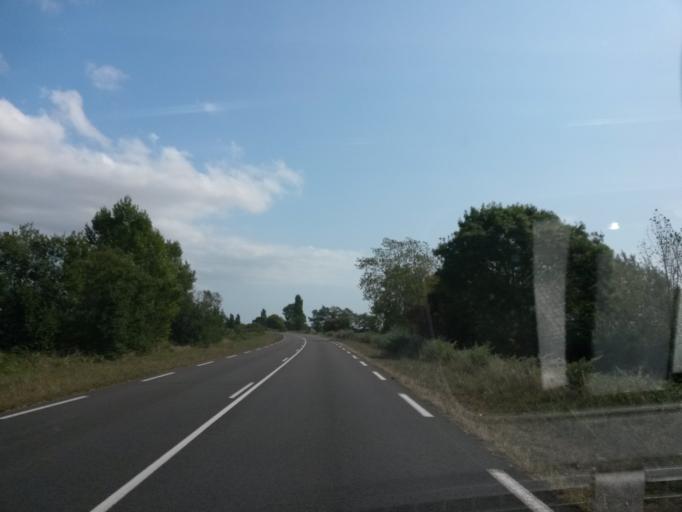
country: FR
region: Pays de la Loire
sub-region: Departement de la Vendee
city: La Tranche-sur-Mer
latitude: 46.3581
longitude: -1.4451
